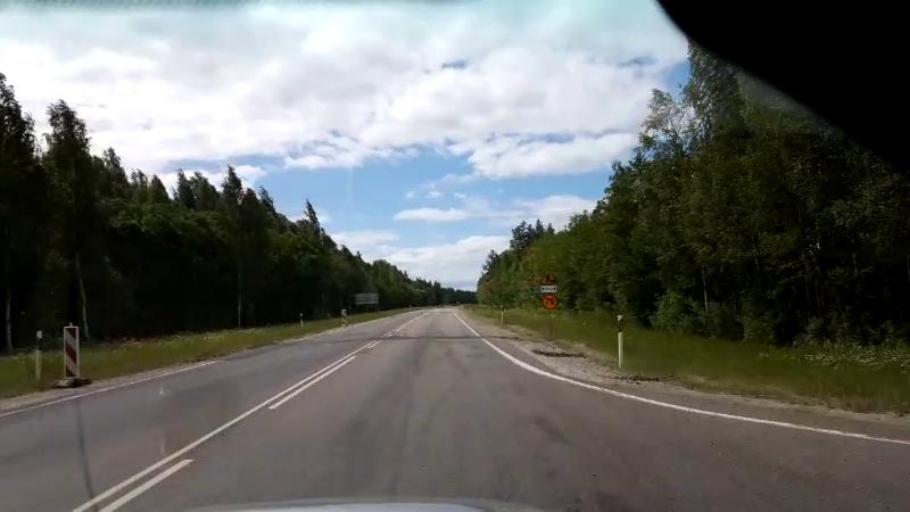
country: LV
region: Salacgrivas
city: Ainazi
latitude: 58.0275
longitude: 24.5030
